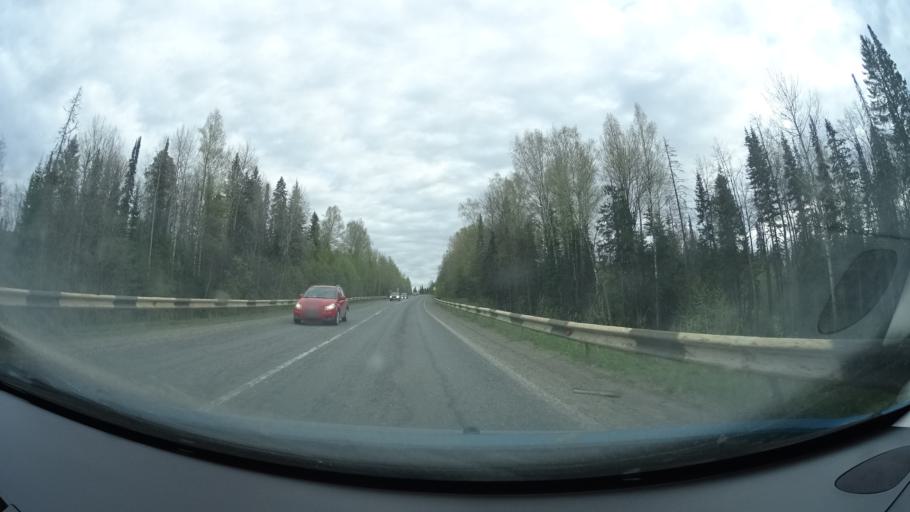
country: RU
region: Perm
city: Yugo-Kamskiy
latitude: 57.6300
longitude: 55.6163
